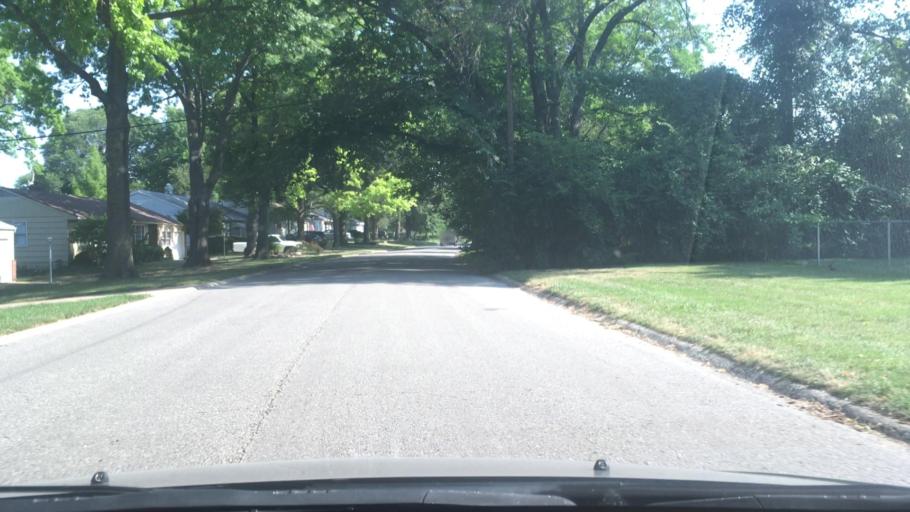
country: US
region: Kansas
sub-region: Johnson County
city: Leawood
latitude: 38.9655
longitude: -94.6011
